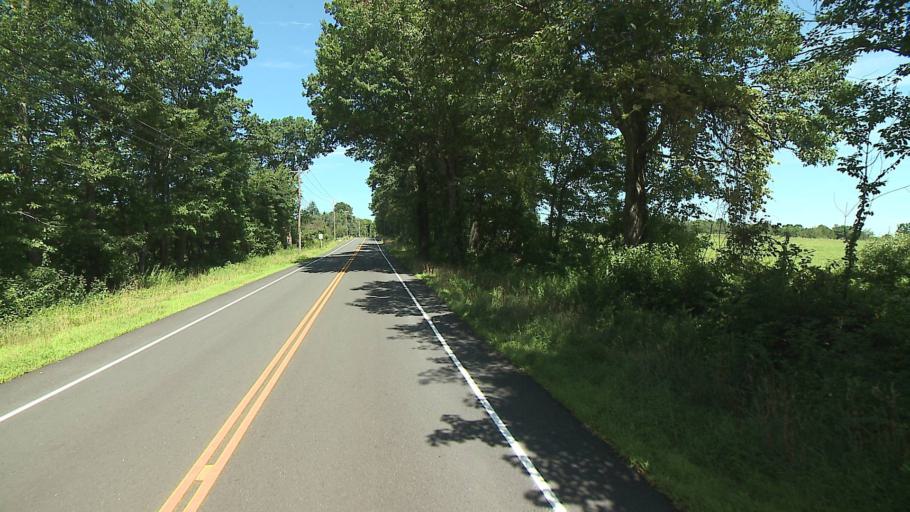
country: US
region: Connecticut
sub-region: Hartford County
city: North Granby
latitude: 41.9674
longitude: -72.9163
